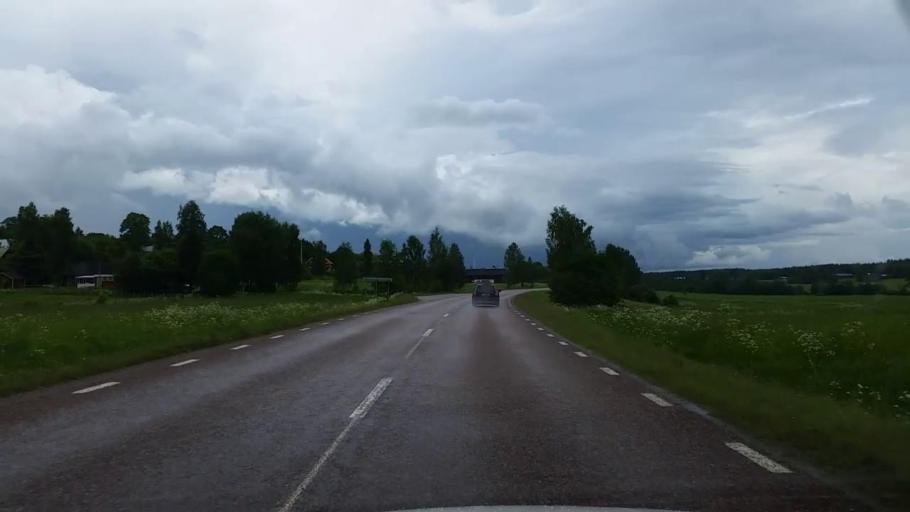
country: SE
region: Gaevleborg
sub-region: Sandvikens Kommun
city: Jarbo
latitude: 60.6907
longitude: 16.6120
